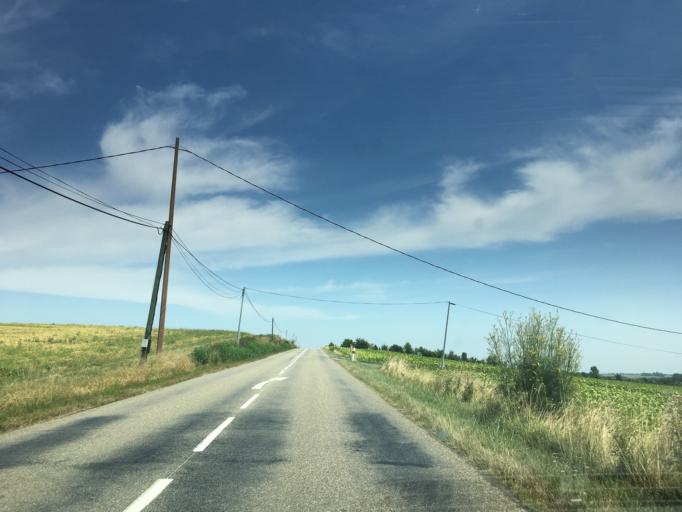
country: FR
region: Midi-Pyrenees
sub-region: Departement du Gers
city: Fleurance
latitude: 43.8630
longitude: 0.7194
